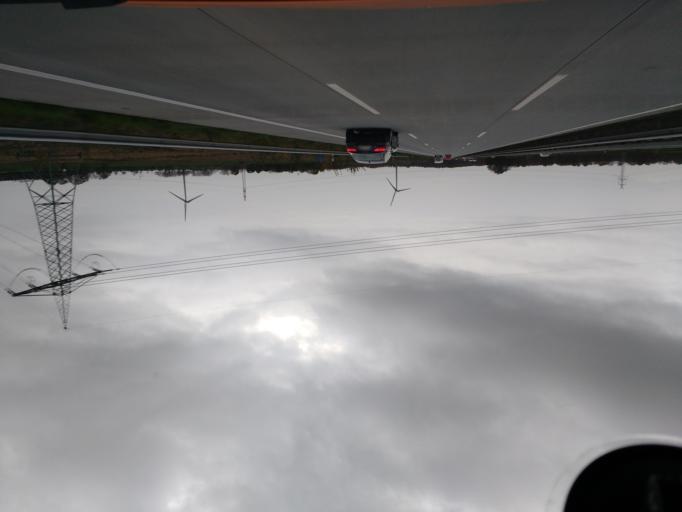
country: DE
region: Lower Saxony
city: Reessum
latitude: 53.1495
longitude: 9.2296
